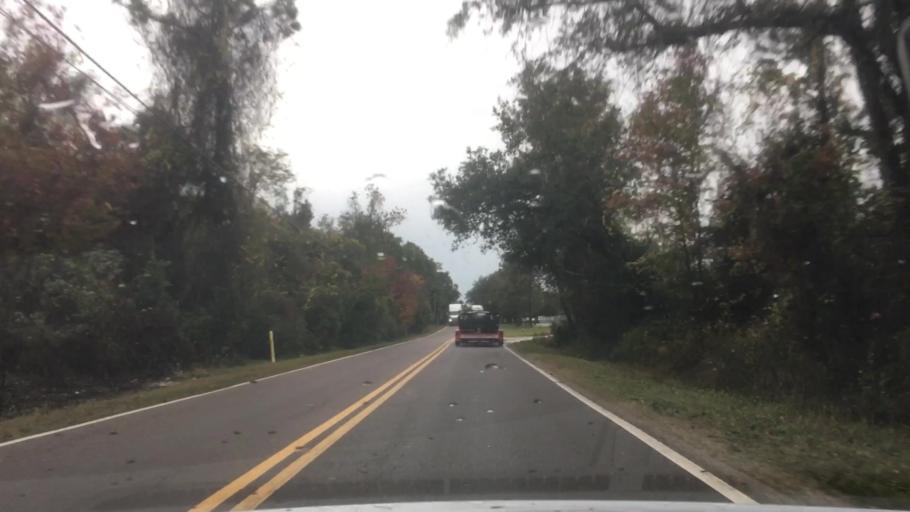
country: US
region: Florida
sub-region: Duval County
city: Jacksonville
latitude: 30.4239
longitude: -81.5639
